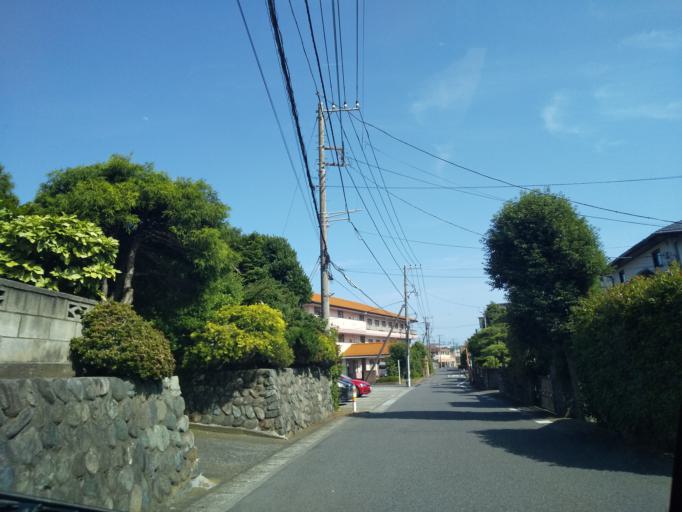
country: JP
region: Kanagawa
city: Minami-rinkan
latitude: 35.4596
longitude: 139.4211
